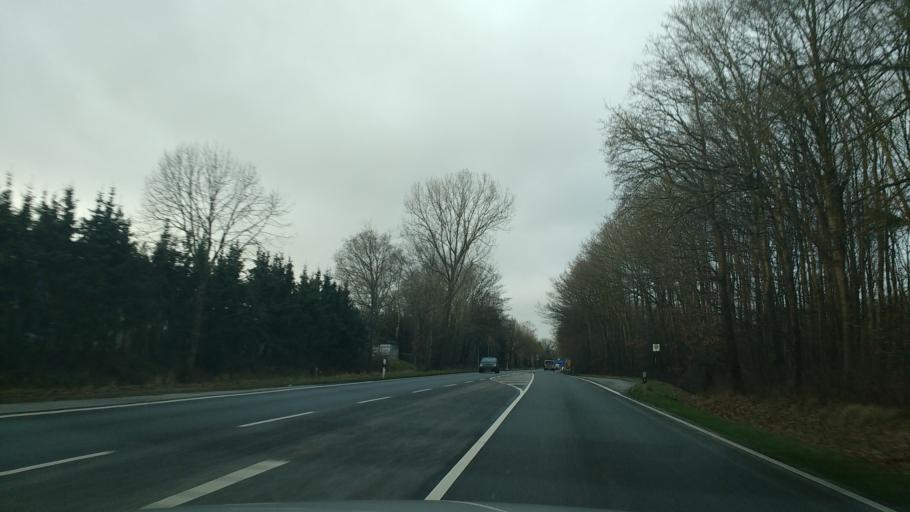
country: DE
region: Schleswig-Holstein
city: Itzehoe
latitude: 53.9013
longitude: 9.5104
